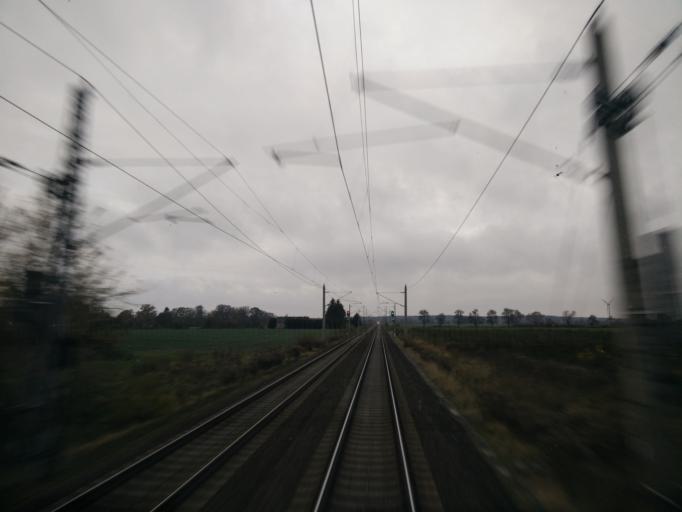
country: DE
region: Brandenburg
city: Kyritz
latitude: 52.8817
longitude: 12.3812
